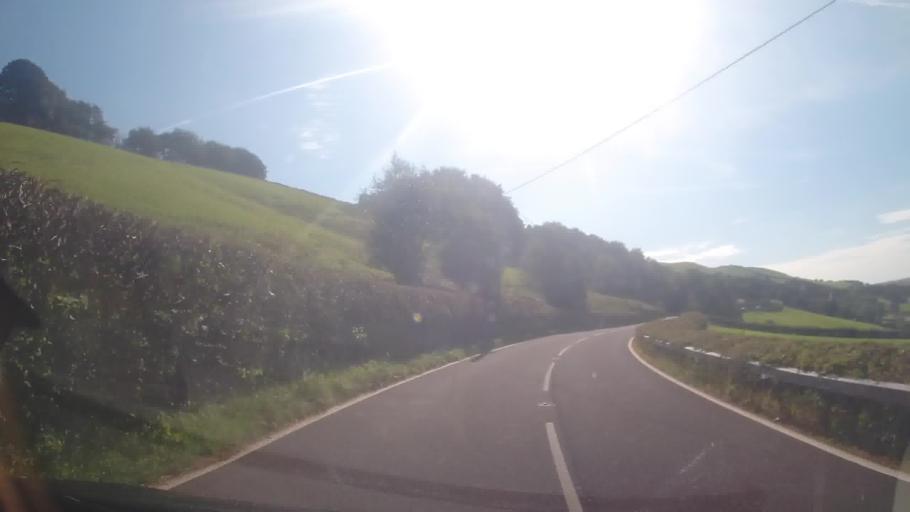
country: GB
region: Wales
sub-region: Sir Powys
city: Mochdre
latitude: 52.4708
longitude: -3.3194
